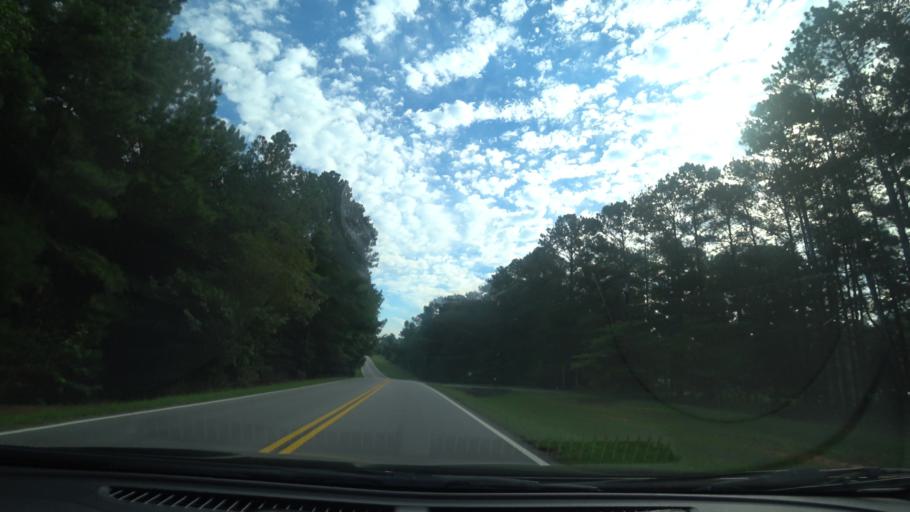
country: US
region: Georgia
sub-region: Rockdale County
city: Lakeview Estates
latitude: 33.7289
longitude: -83.9980
